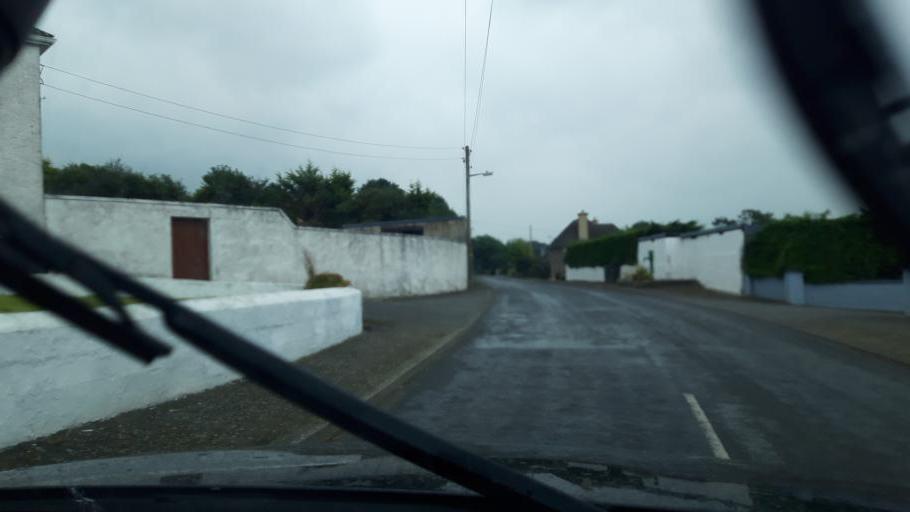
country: IE
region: Leinster
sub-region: Kilkenny
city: Callan
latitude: 52.6621
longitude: -7.4382
